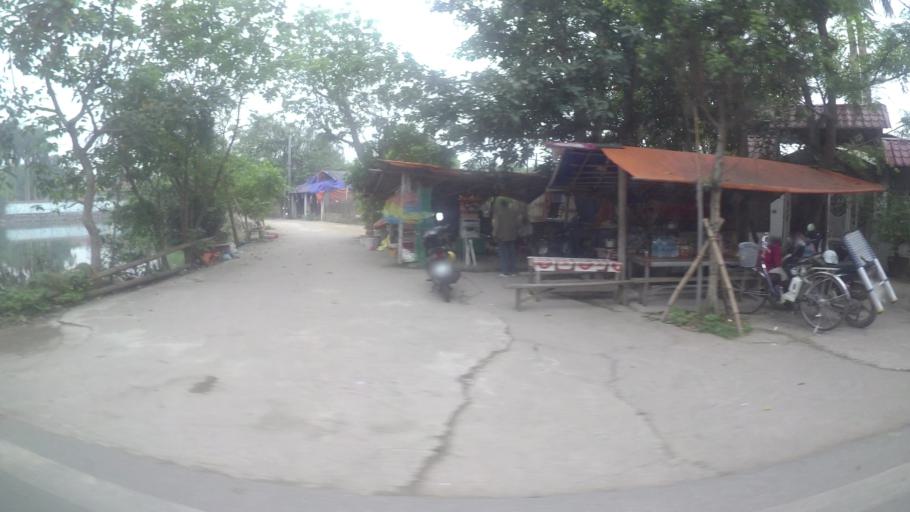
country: VN
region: Ha Noi
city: Tay Ho
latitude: 21.0615
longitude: 105.8239
